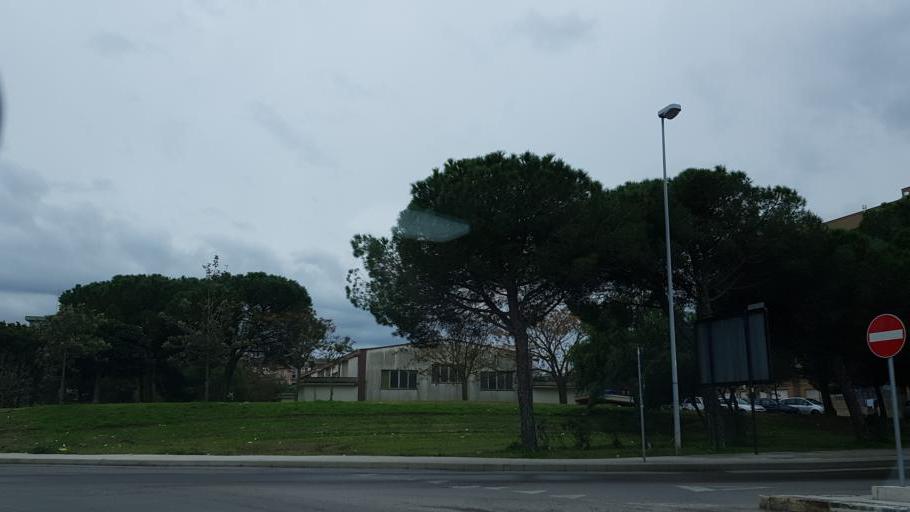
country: IT
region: Apulia
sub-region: Provincia di Brindisi
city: Brindisi
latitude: 40.6214
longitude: 17.9183
